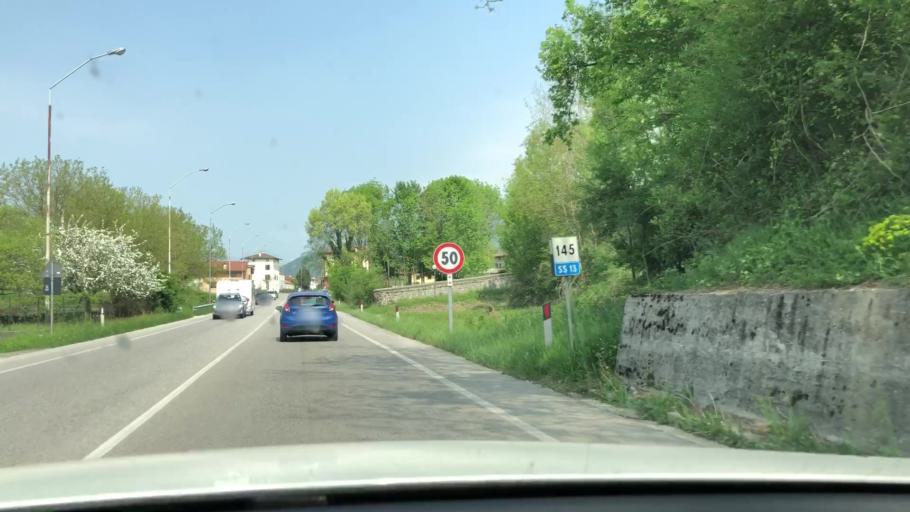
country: IT
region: Friuli Venezia Giulia
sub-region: Provincia di Udine
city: Cassacco
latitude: 46.1944
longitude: 13.1943
